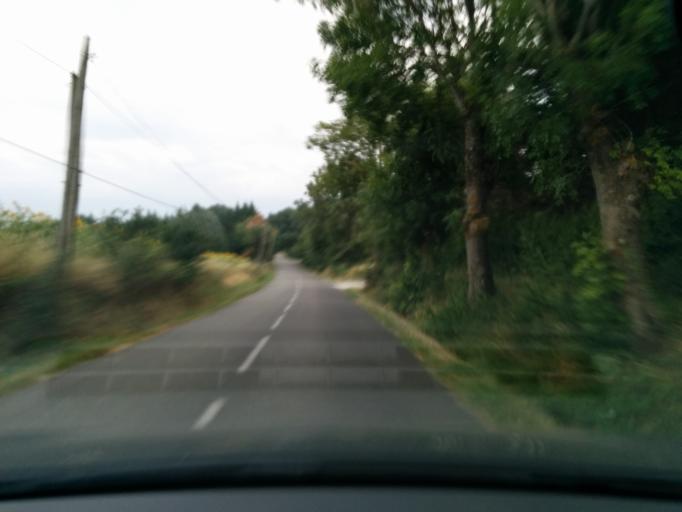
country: FR
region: Midi-Pyrenees
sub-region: Departement de la Haute-Garonne
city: Castanet-Tolosan
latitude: 43.5063
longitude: 1.4861
